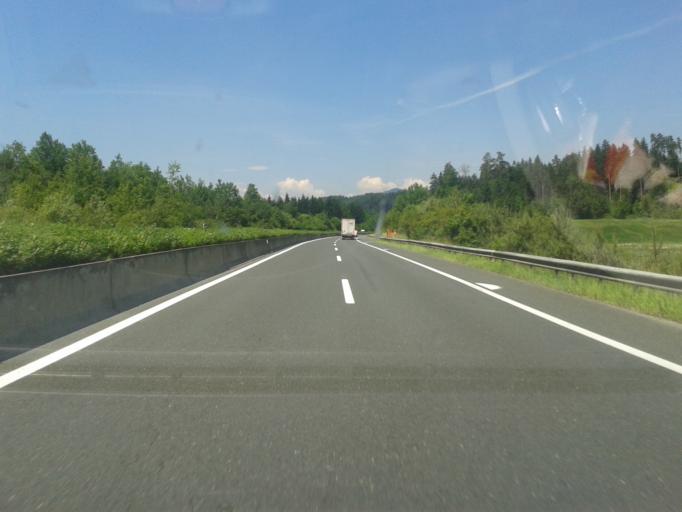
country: AT
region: Carinthia
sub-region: Politischer Bezirk Klagenfurt Land
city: Grafenstein
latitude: 46.6482
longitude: 14.5435
